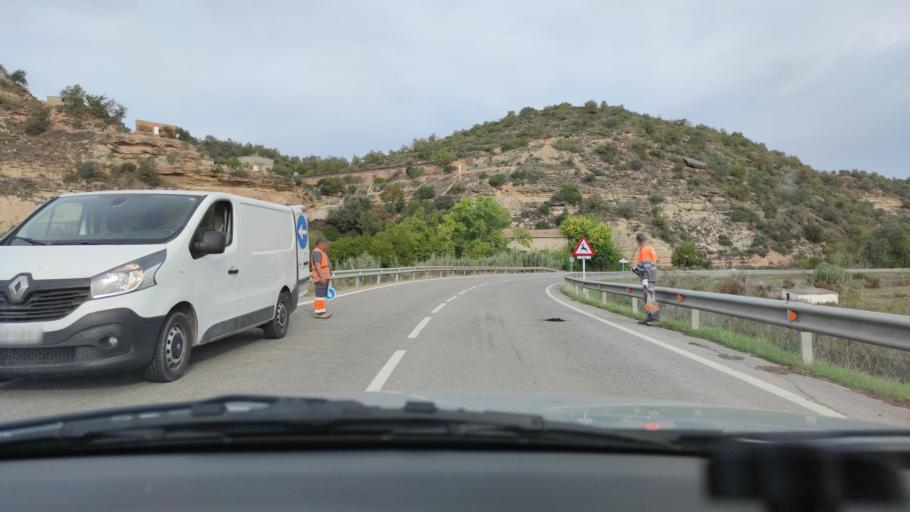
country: ES
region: Catalonia
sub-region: Provincia de Lleida
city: Artesa de Segre
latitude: 41.9108
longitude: 1.0680
